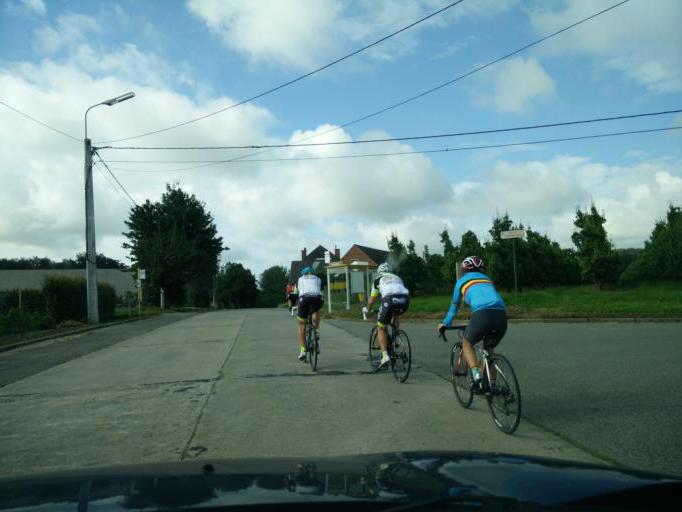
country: BE
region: Wallonia
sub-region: Province du Hainaut
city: Flobecq
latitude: 50.7739
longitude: 3.7331
